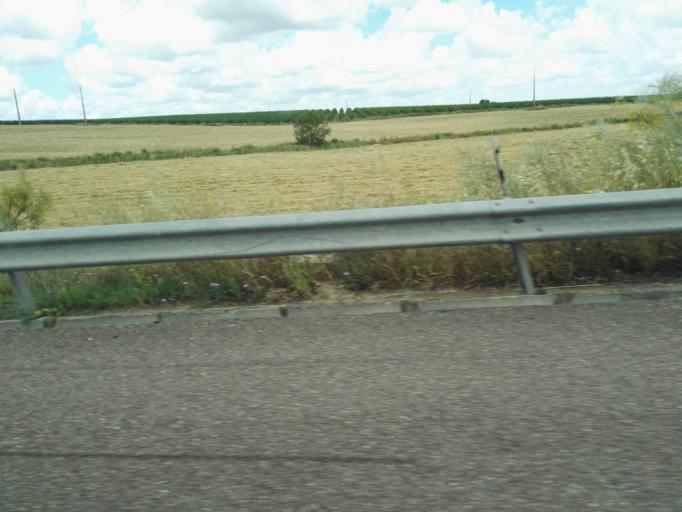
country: PT
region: Portalegre
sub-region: Elvas
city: Elvas
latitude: 38.8890
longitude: -7.1056
